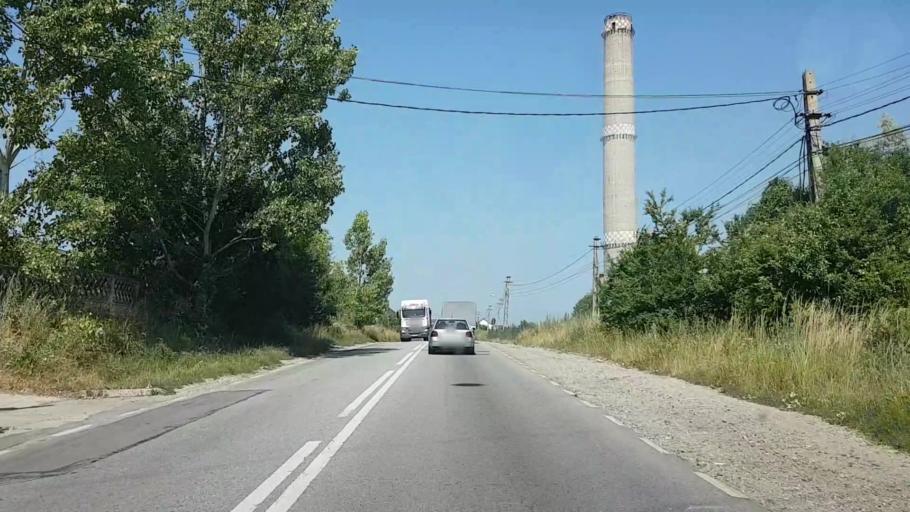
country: RO
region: Cluj
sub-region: Comuna Cusdrioara
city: Cusdrioara
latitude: 47.1618
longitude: 23.8934
